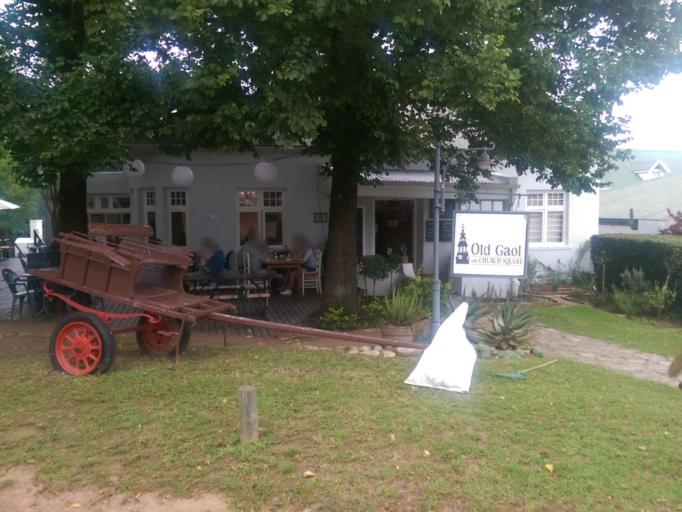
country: ZA
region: Western Cape
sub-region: Overberg District Municipality
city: Swellendam
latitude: -34.0180
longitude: 20.4472
